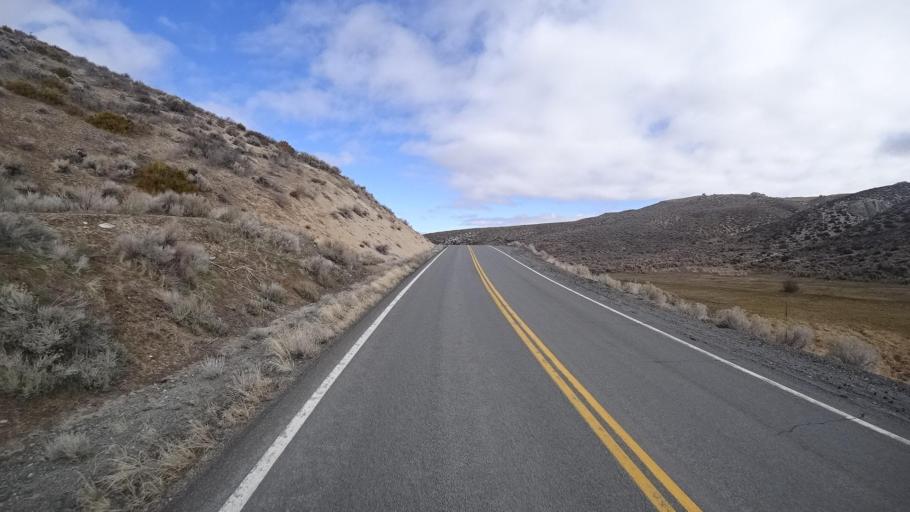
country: US
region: Nevada
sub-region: Washoe County
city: Cold Springs
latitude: 39.8123
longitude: -119.9339
